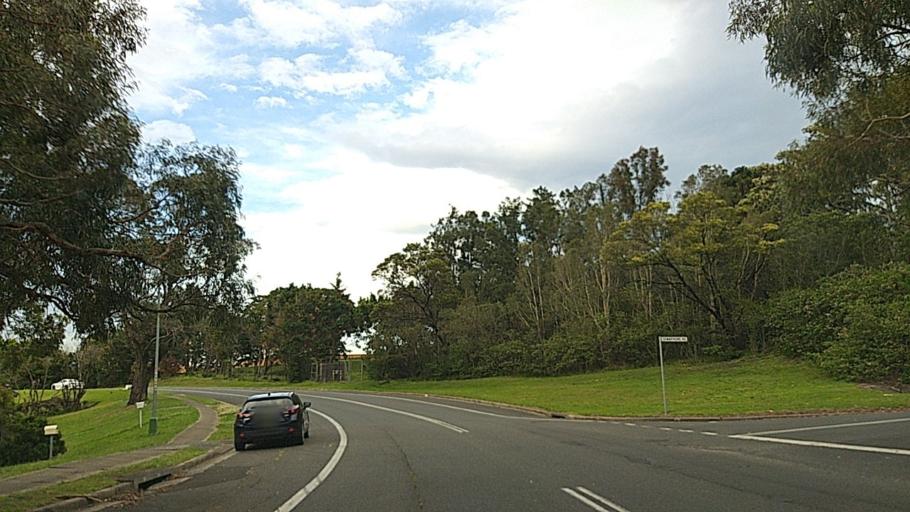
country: AU
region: New South Wales
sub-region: Wollongong
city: Berkeley
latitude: -34.4682
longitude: 150.8460
